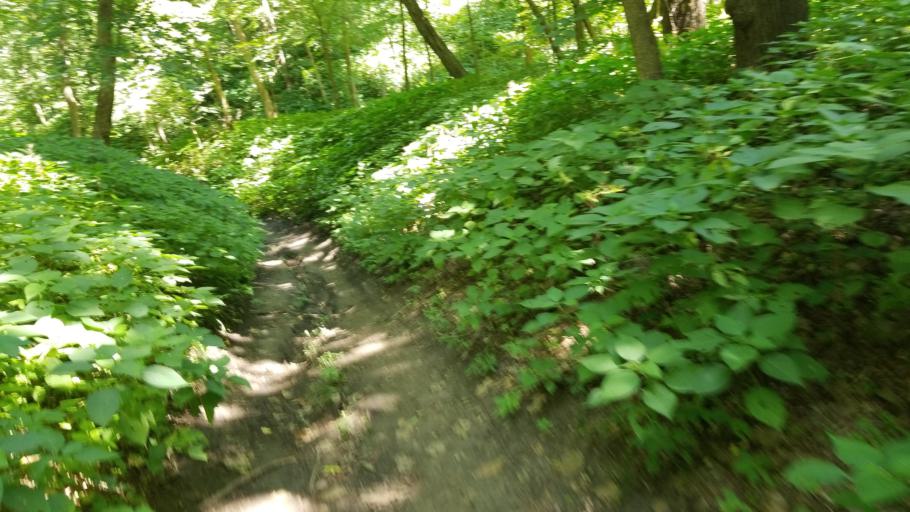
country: US
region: Iowa
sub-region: Pottawattamie County
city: Carter Lake
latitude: 41.3954
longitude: -95.9561
